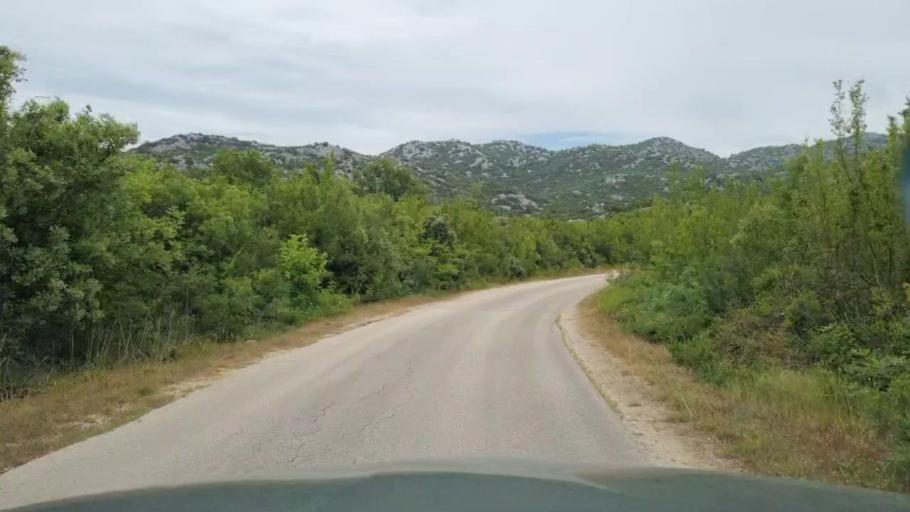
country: BA
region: Federation of Bosnia and Herzegovina
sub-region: Hercegovacko-Bosanski Kanton
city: Neum
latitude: 42.9255
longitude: 17.6779
